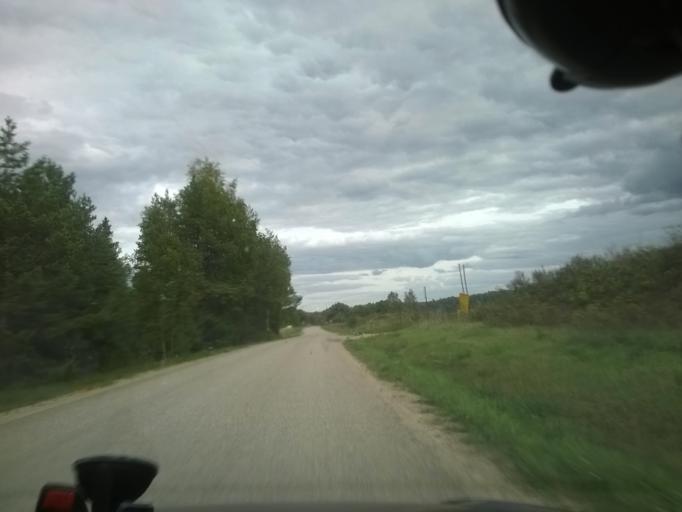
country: EE
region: Vorumaa
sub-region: Voru linn
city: Voru
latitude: 57.8200
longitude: 27.1219
